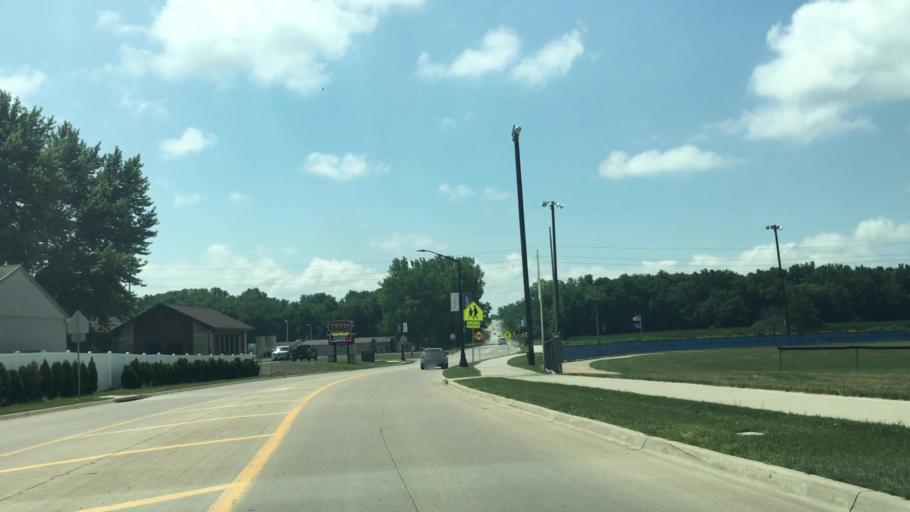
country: US
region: Iowa
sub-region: Johnson County
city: Tiffin
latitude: 41.7051
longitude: -91.6666
